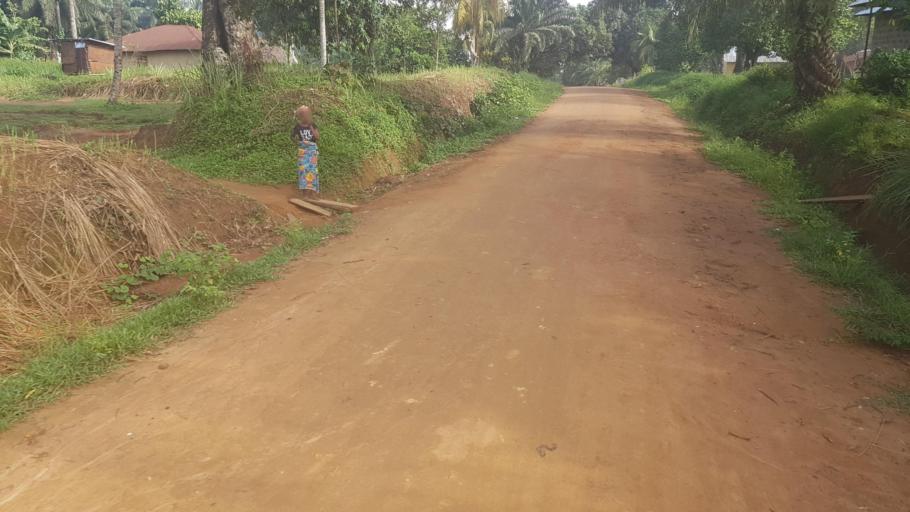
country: SL
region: Southern Province
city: Sumbuya
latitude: 7.6134
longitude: -12.1421
